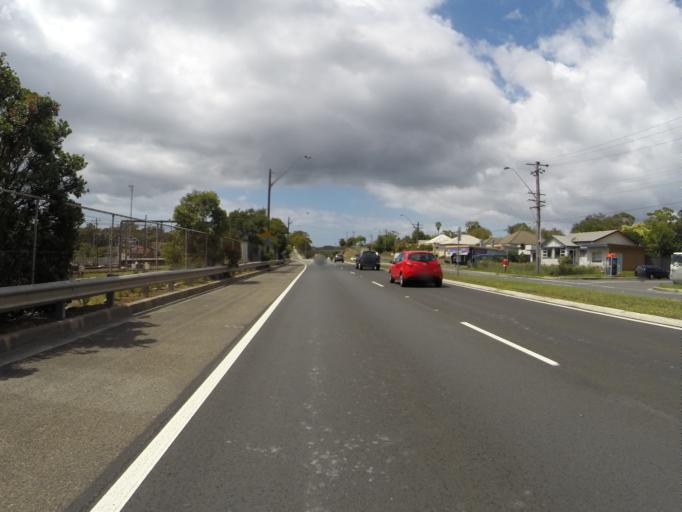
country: AU
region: New South Wales
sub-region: Wollongong
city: Helensburgh
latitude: -34.1327
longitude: 150.9938
